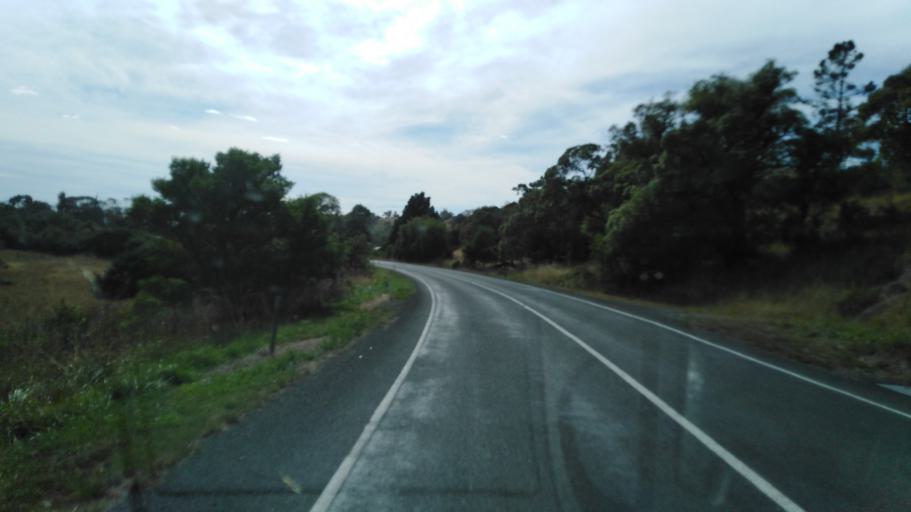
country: NZ
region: Canterbury
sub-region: Kaikoura District
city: Kaikoura
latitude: -42.5180
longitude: 173.4990
